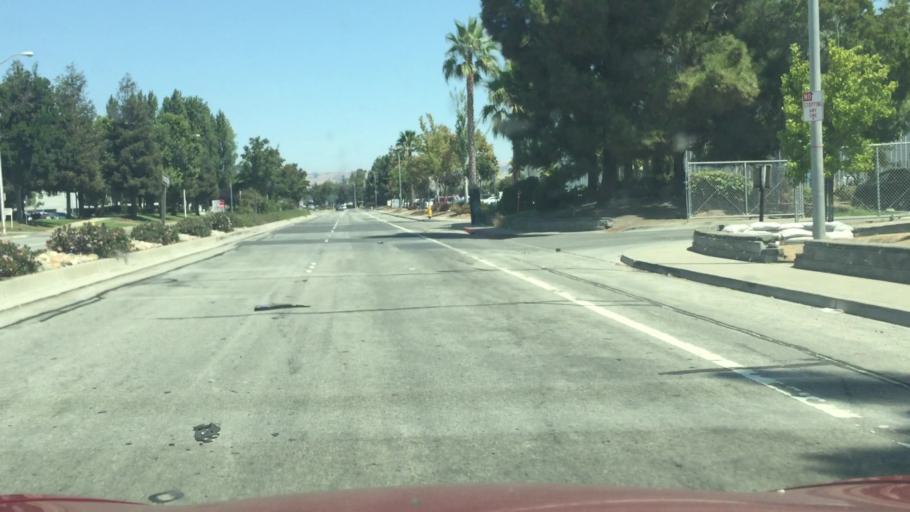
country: US
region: California
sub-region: Alameda County
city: Fremont
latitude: 37.5078
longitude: -121.9964
